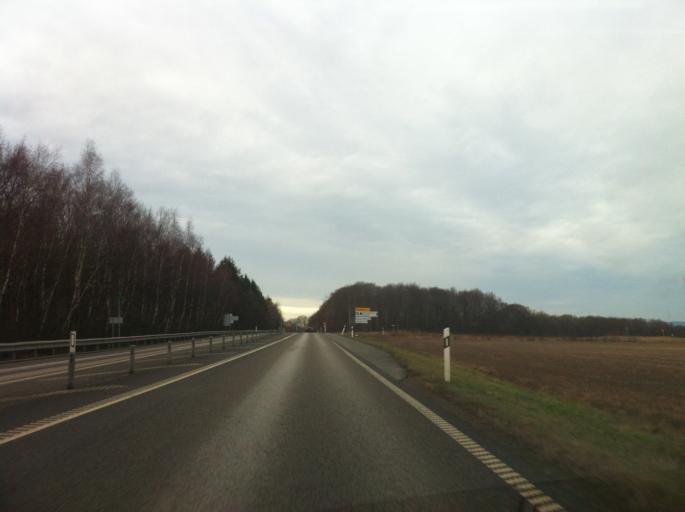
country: DK
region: Capital Region
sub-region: Helsingor Kommune
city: Hellebaek
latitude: 56.1210
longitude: 12.6234
